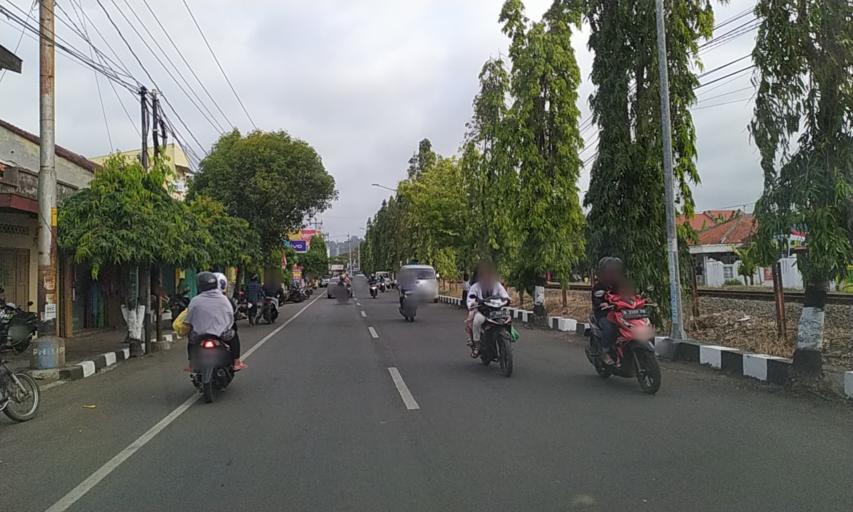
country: ID
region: Central Java
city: Karangbadar Kidul
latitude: -7.7314
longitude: 109.0072
